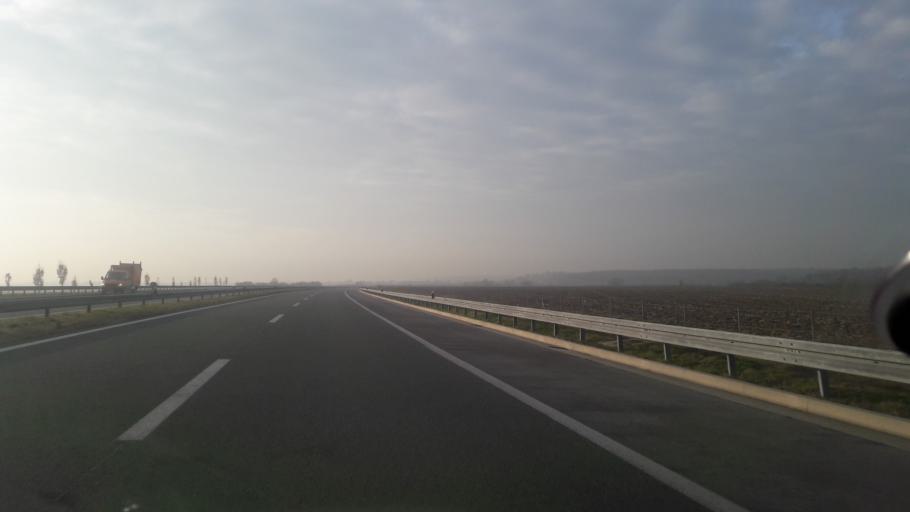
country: HR
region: Osjecko-Baranjska
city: Gorjani
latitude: 45.3477
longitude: 18.4007
